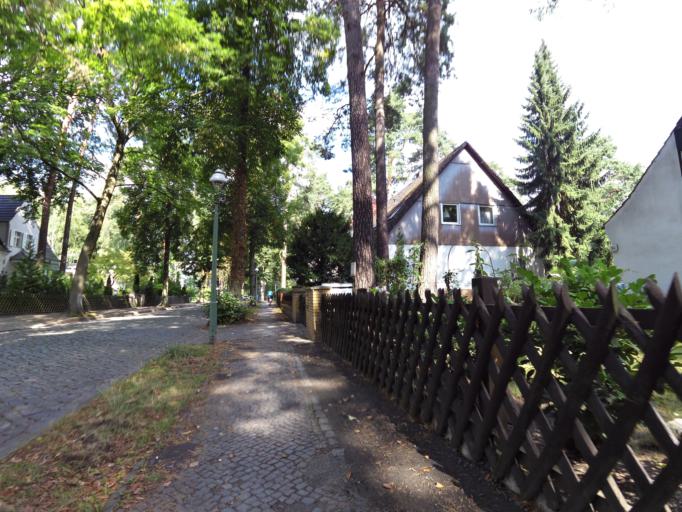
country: DE
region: Berlin
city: Lichtenrade
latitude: 52.3785
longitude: 13.3999
